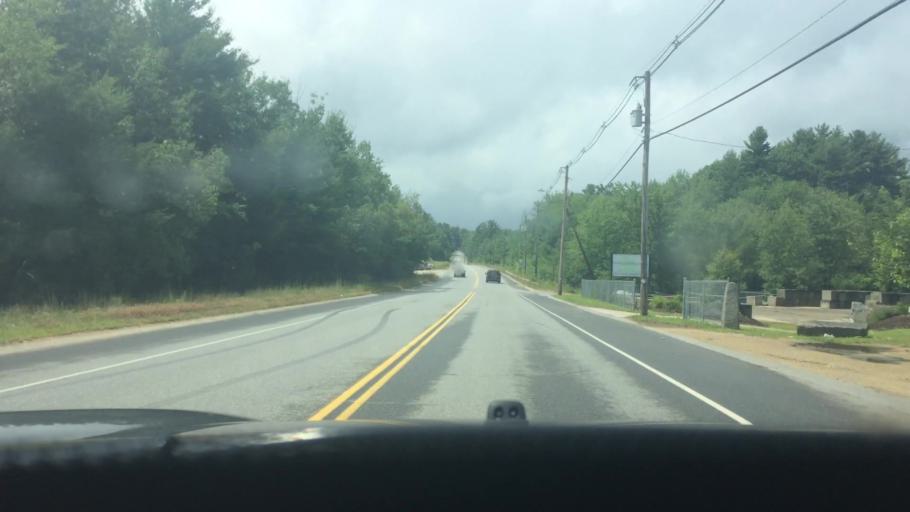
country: US
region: Massachusetts
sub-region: Worcester County
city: Gardner
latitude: 42.5705
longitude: -72.0256
